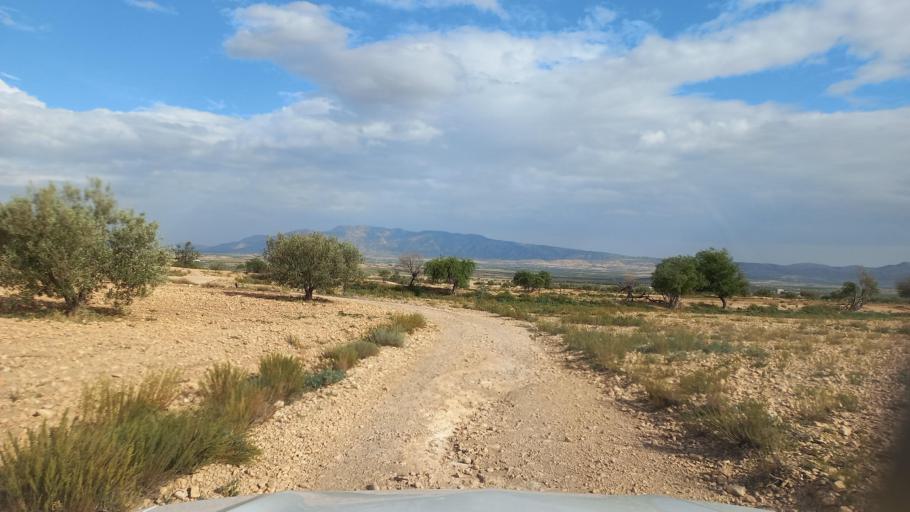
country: TN
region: Al Qasrayn
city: Sbiba
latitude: 35.4515
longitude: 9.0763
